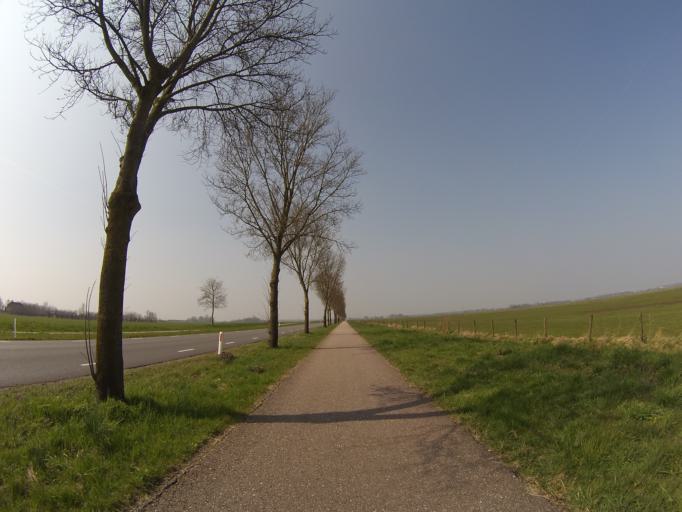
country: NL
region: Utrecht
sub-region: Gemeente Bunschoten
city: Bunschoten
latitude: 52.2280
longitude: 5.4191
